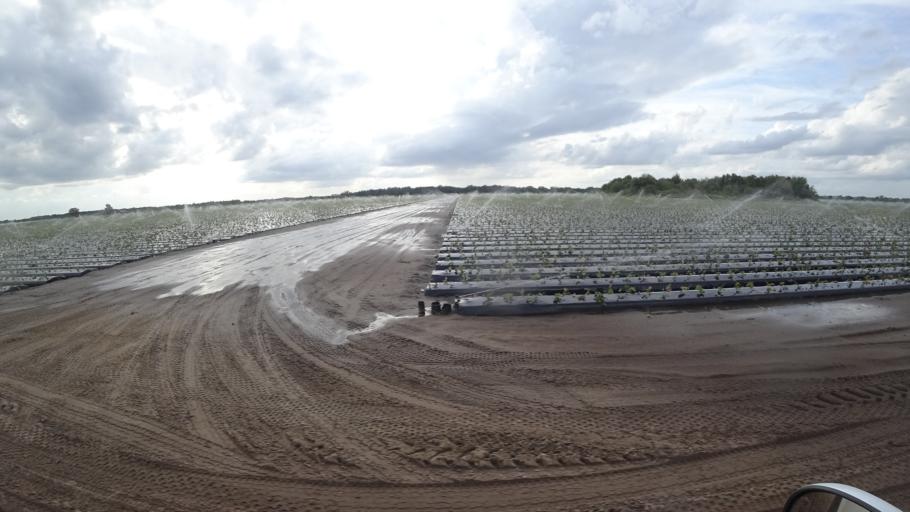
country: US
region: Florida
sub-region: Hillsborough County
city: Wimauma
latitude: 27.5751
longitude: -82.1573
